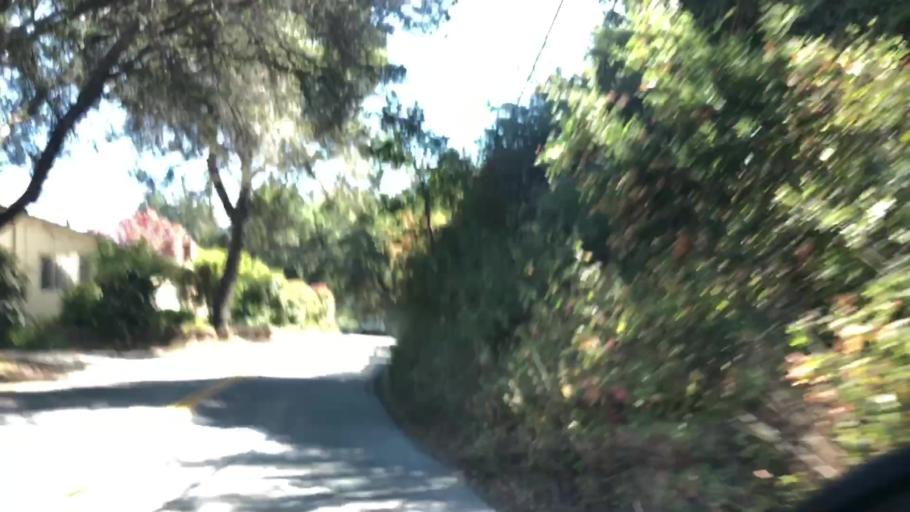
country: US
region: California
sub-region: Santa Cruz County
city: Corralitos
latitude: 36.9887
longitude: -121.8320
